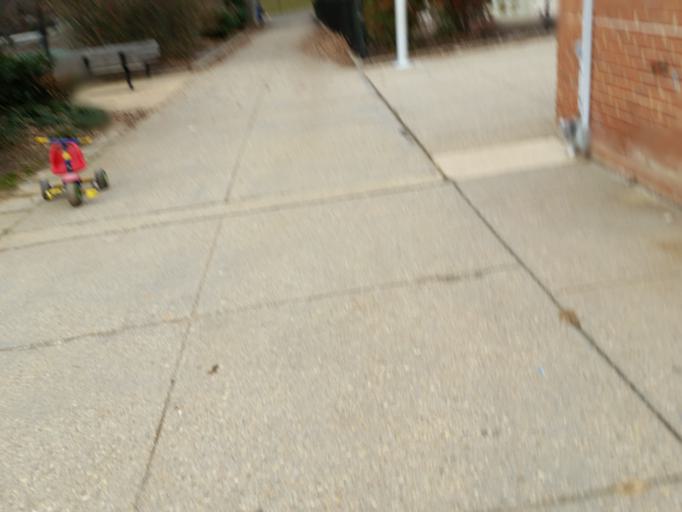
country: US
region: Maryland
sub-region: Montgomery County
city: Friendship Village
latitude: 38.9426
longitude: -77.0884
